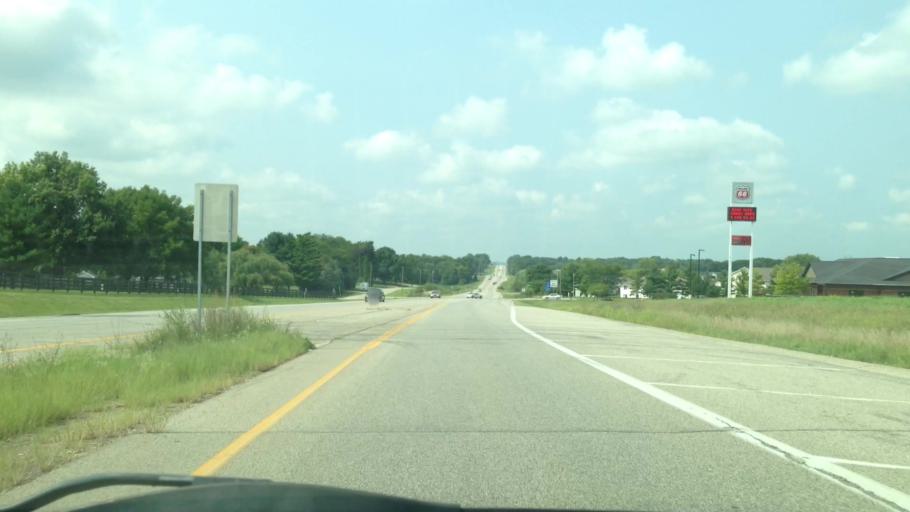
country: US
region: Iowa
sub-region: Linn County
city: Fairfax
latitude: 41.9435
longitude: -91.7452
